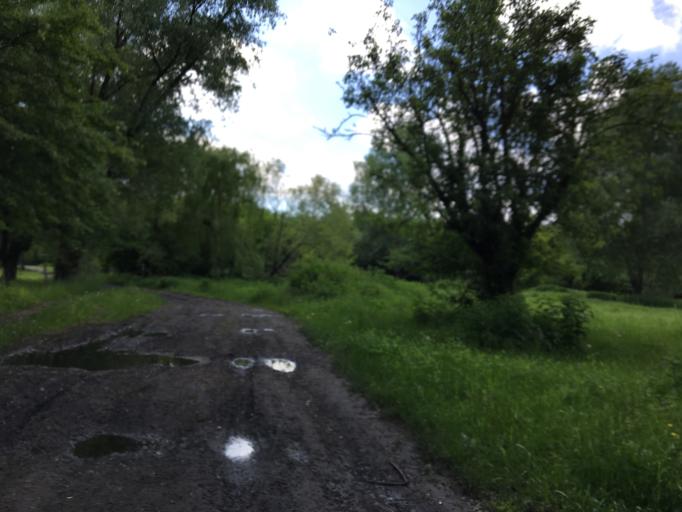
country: HU
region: Pest
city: Urom
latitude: 47.5749
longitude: 19.0412
